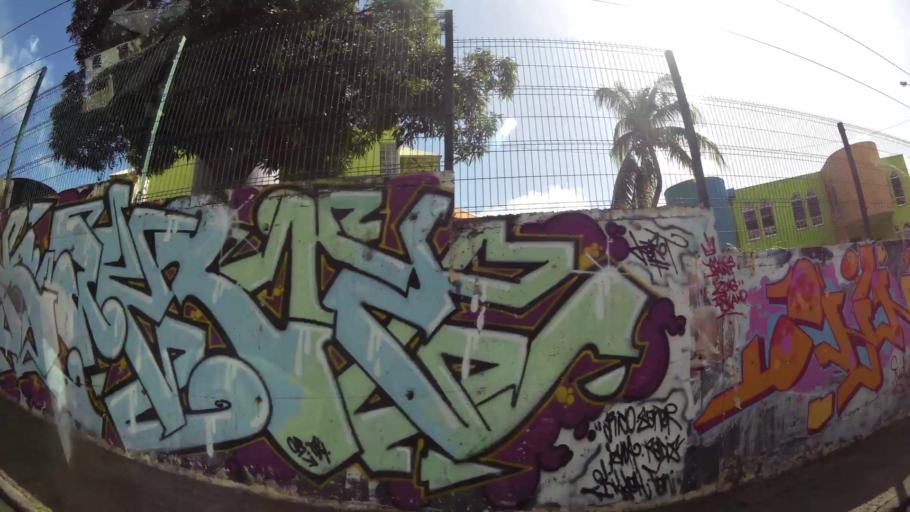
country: MQ
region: Martinique
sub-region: Martinique
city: Fort-de-France
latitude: 14.6082
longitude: -61.0608
